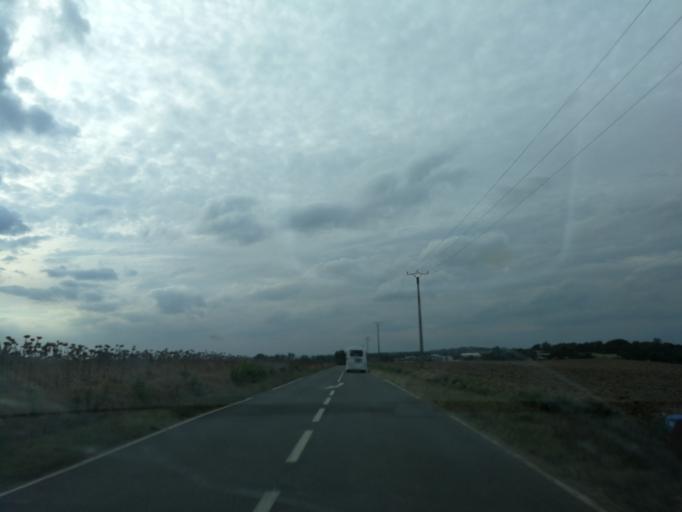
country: FR
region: Midi-Pyrenees
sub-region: Departement de la Haute-Garonne
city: Flourens
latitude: 43.5953
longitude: 1.5551
